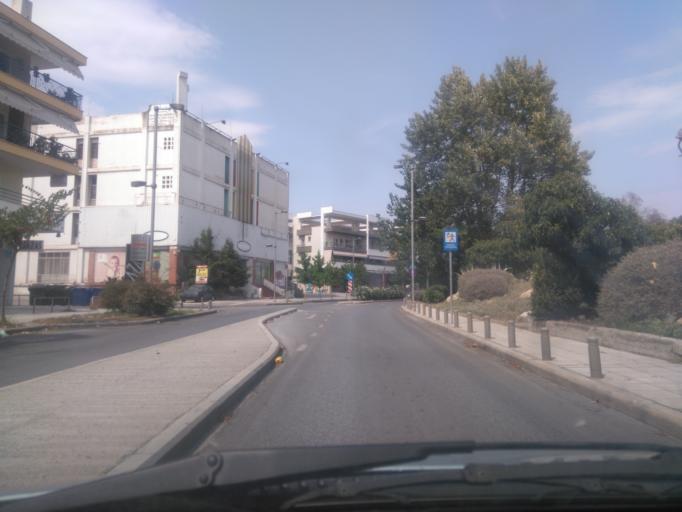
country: GR
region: Central Macedonia
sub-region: Nomos Thessalonikis
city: Ampelokipoi
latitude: 40.6610
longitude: 22.9277
